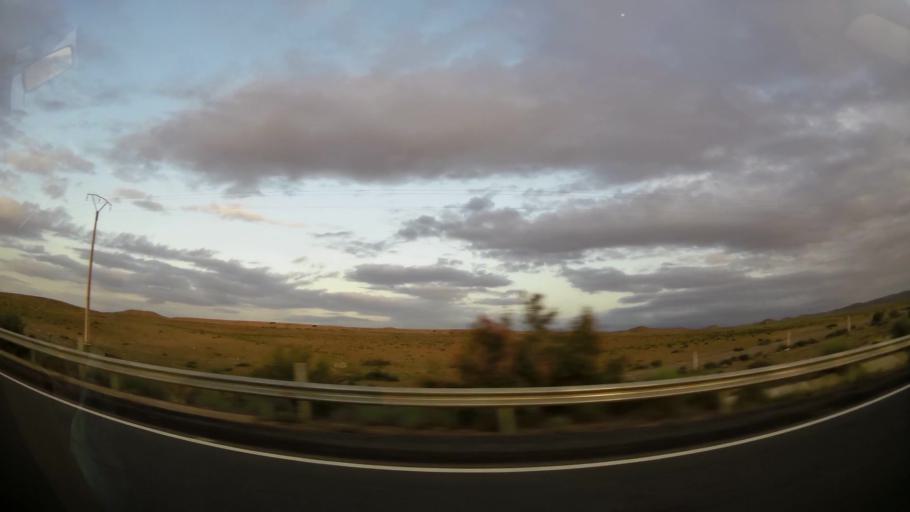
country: MA
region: Oriental
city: Taourirt
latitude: 34.5319
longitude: -2.9194
